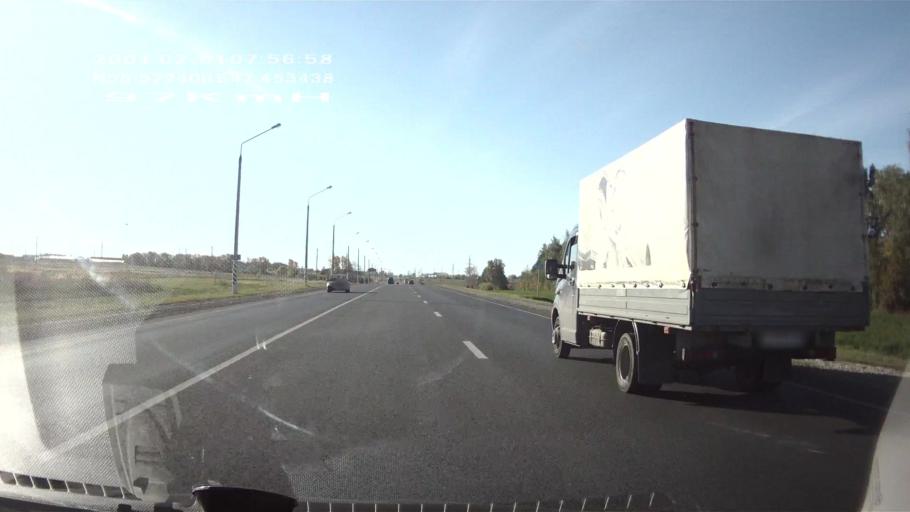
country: RU
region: Chuvashia
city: Kanash
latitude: 55.5229
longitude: 47.4548
